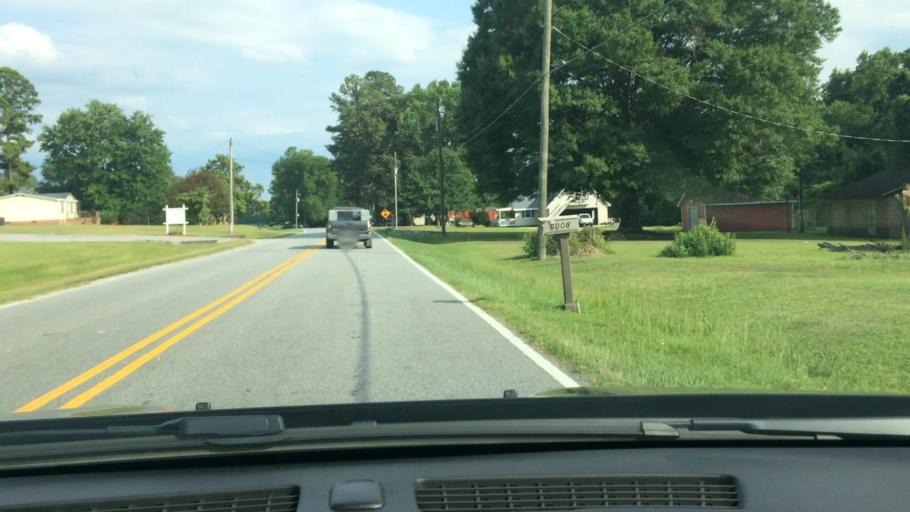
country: US
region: North Carolina
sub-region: Pitt County
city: Ayden
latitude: 35.4899
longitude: -77.3762
